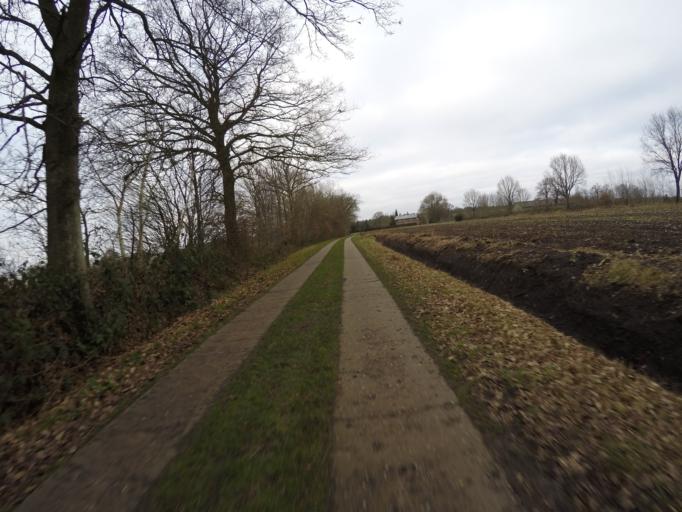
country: DE
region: Schleswig-Holstein
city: Hemdingen
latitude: 53.7855
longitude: 9.8343
